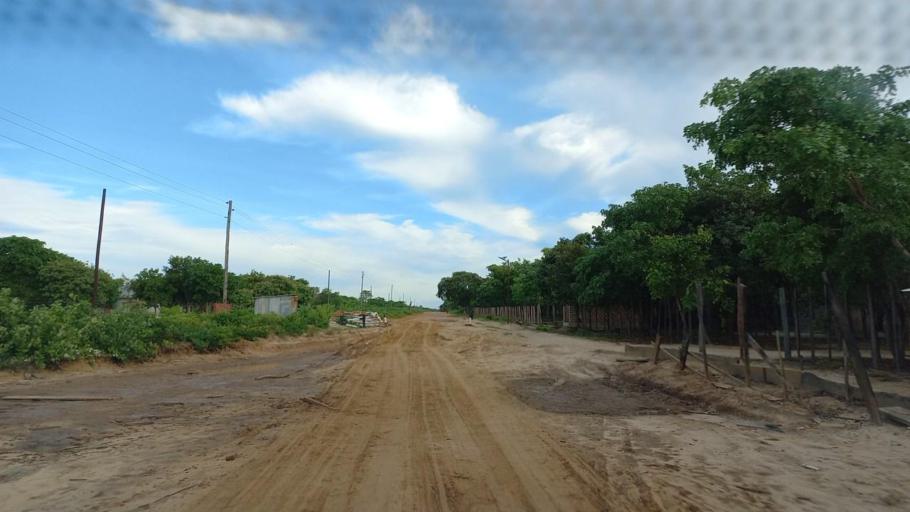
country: ZM
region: North-Western
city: Kabompo
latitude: -13.4140
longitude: 24.3179
